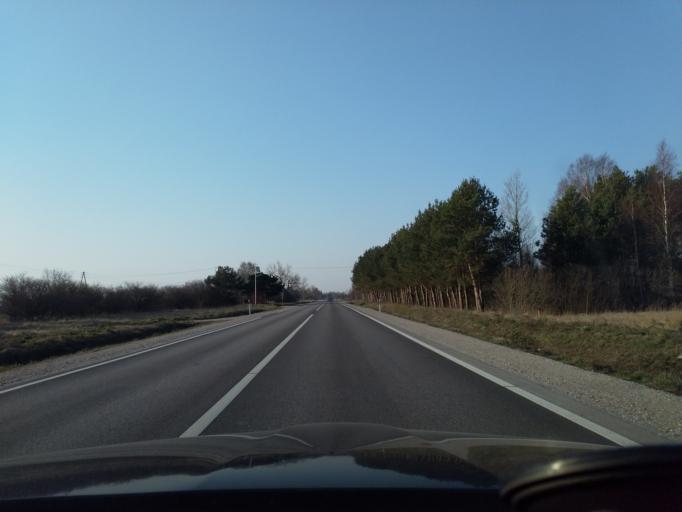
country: LV
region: Liepaja
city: Liepaja
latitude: 56.4615
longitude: 21.0136
